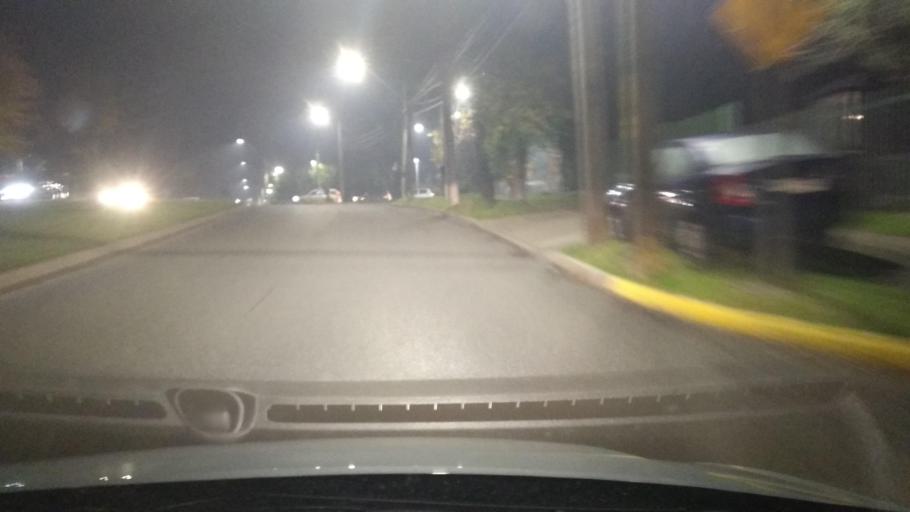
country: CL
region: Los Rios
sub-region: Provincia de Valdivia
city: Valdivia
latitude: -39.8085
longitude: -73.2563
